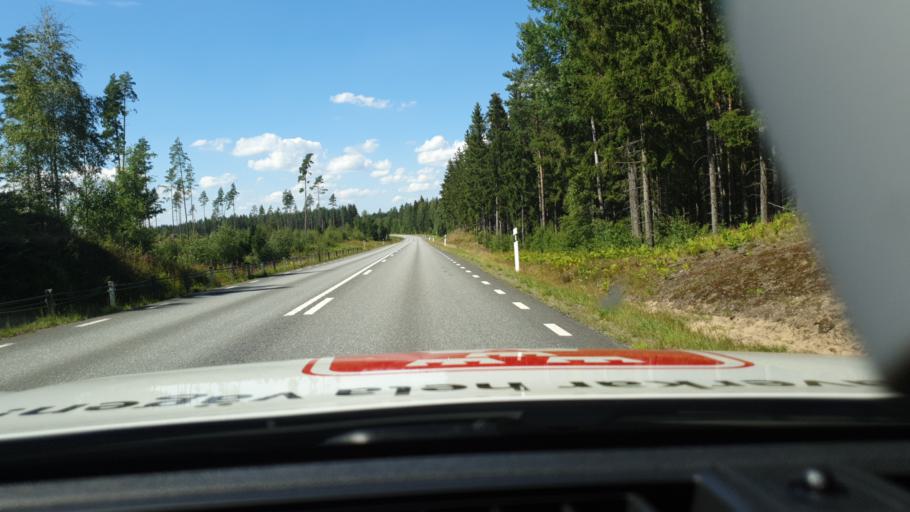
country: SE
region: Joenkoeping
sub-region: Savsjo Kommun
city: Vrigstad
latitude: 57.3710
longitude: 14.4183
